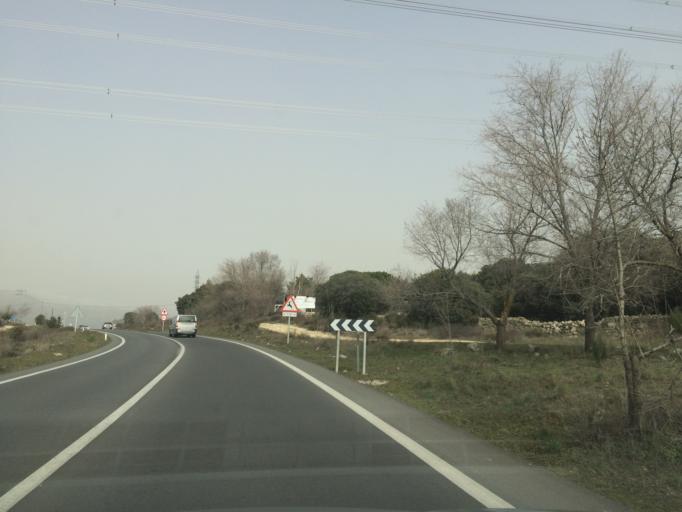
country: ES
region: Madrid
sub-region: Provincia de Madrid
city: Collado-Villalba
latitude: 40.6498
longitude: -3.9893
